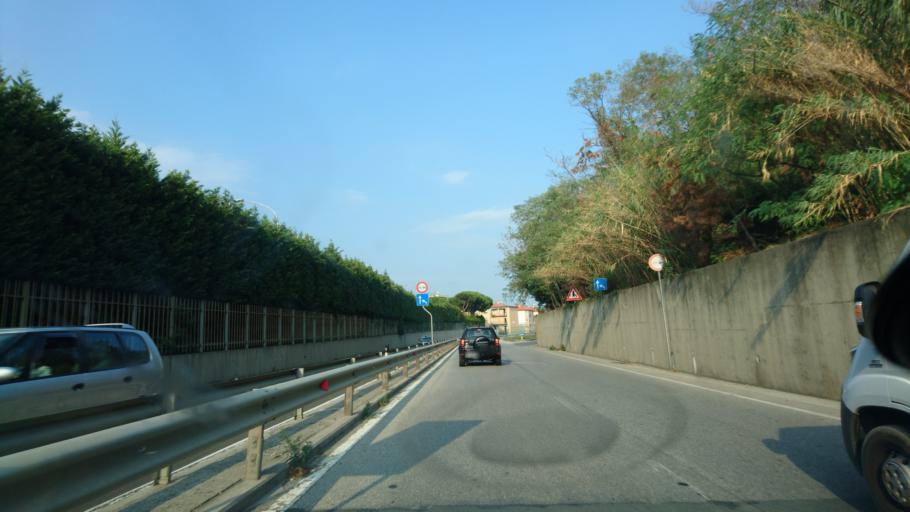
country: IT
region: Liguria
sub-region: Provincia di Savona
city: Vado Ligure
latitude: 44.2730
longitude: 8.4317
